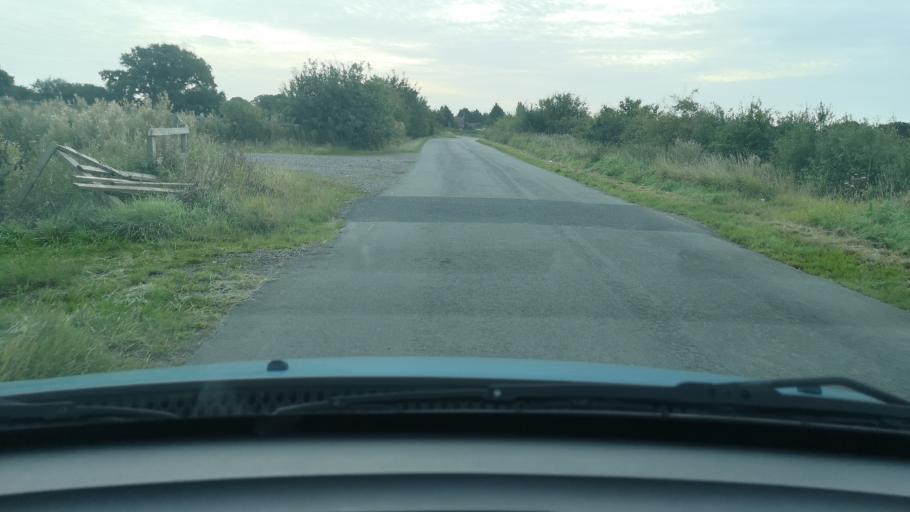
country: GB
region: England
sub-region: Doncaster
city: Stainforth
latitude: 53.6296
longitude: -1.0252
